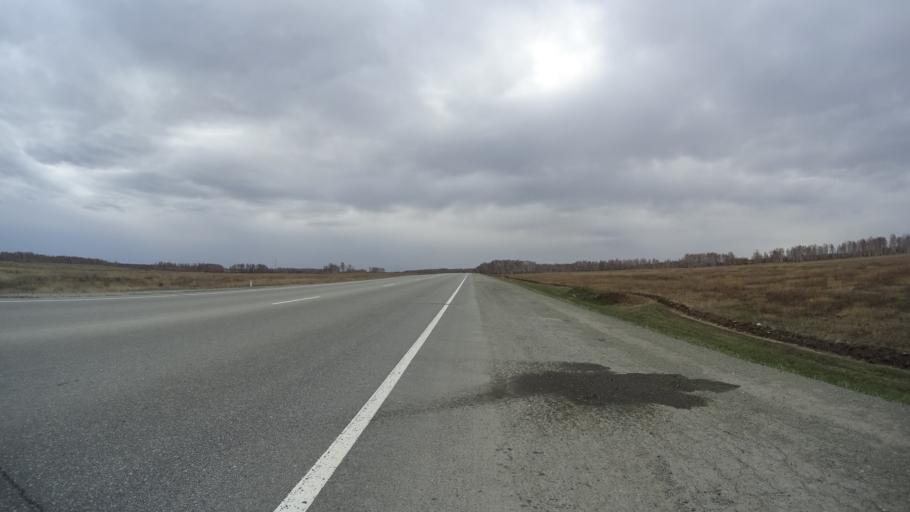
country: RU
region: Chelyabinsk
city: Yemanzhelinsk
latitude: 54.7037
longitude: 61.2549
